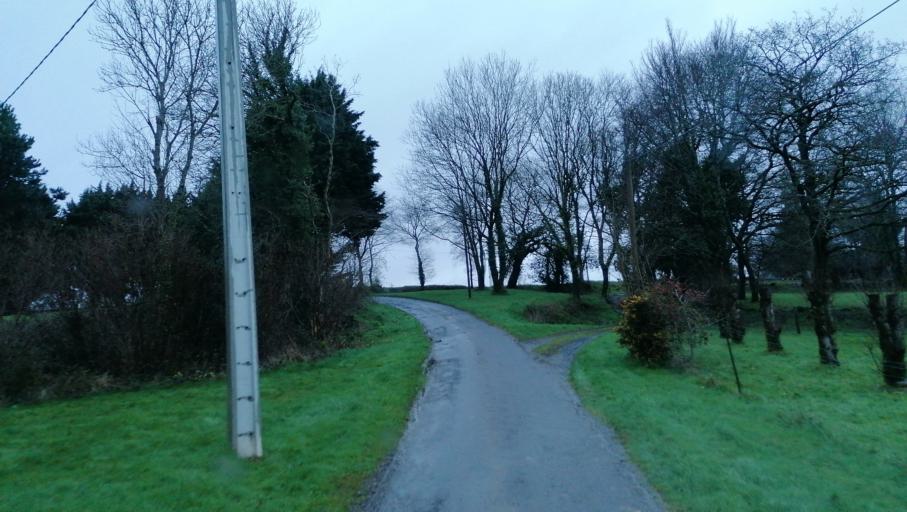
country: FR
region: Brittany
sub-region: Departement des Cotes-d'Armor
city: Lanrodec
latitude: 48.4805
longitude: -2.9992
